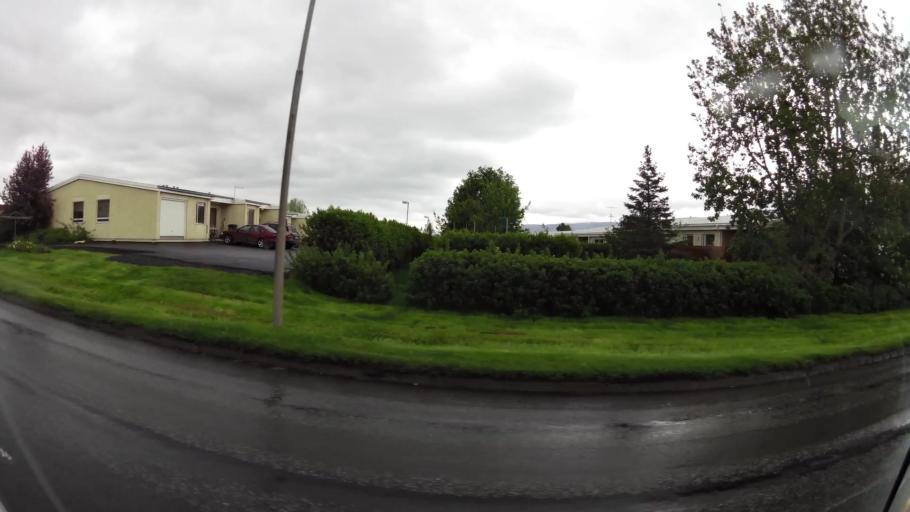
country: IS
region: Northeast
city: Akureyri
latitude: 65.6874
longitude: -18.1343
